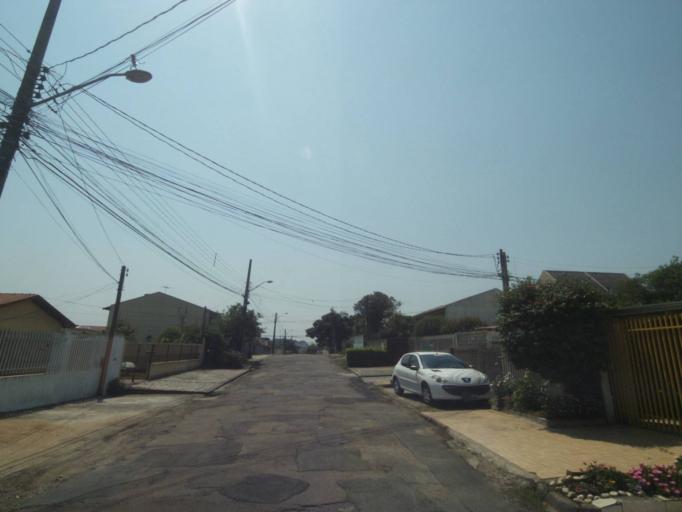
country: BR
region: Parana
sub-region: Sao Jose Dos Pinhais
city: Sao Jose dos Pinhais
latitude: -25.5115
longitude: -49.2665
